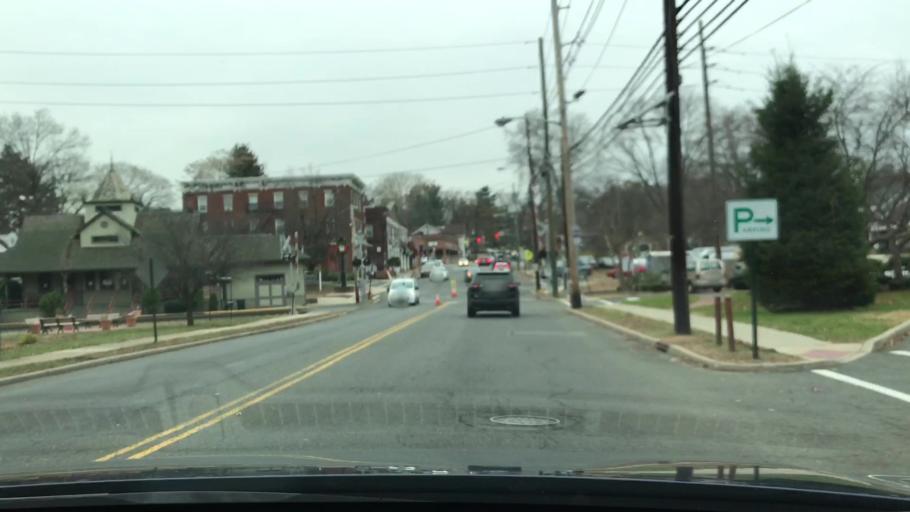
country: US
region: New Jersey
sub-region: Bergen County
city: Oradell
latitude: 40.9539
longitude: -74.0293
